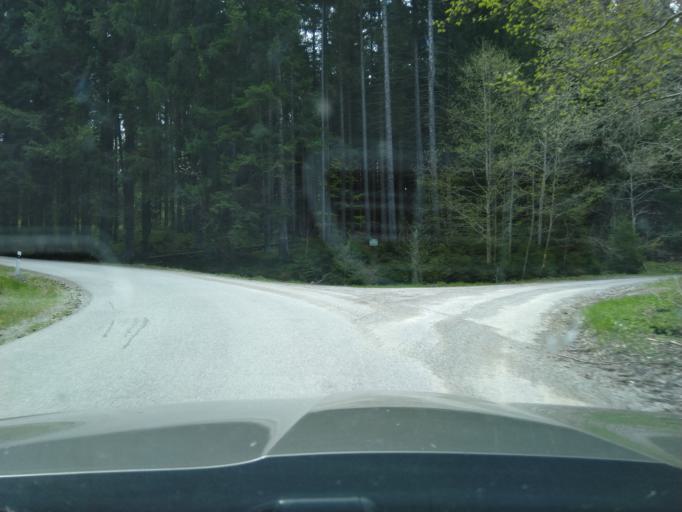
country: CZ
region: Jihocesky
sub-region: Okres Prachatice
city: Vimperk
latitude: 49.0175
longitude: 13.7258
